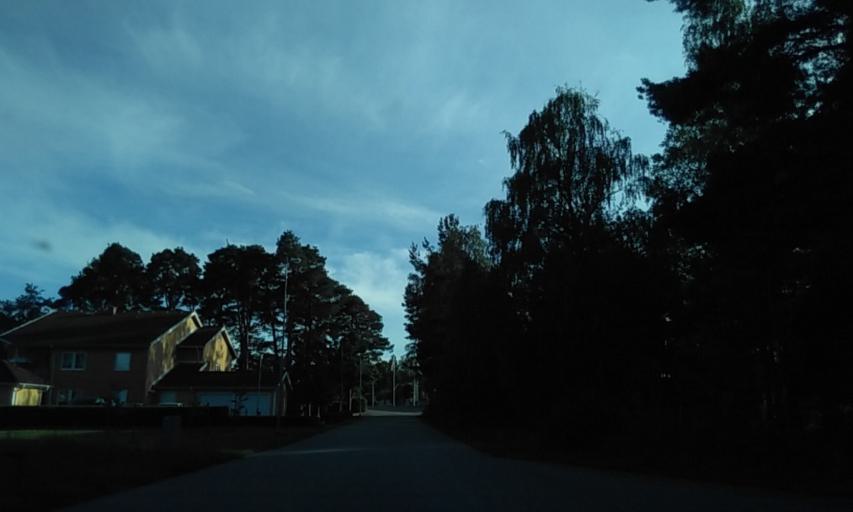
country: SE
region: Vaestra Goetaland
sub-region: Vara Kommun
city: Vara
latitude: 58.3269
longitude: 12.9247
